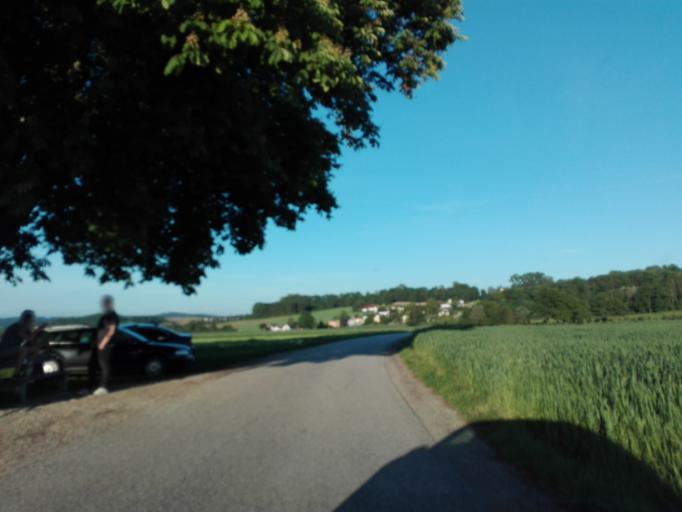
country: AT
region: Upper Austria
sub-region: Politischer Bezirk Urfahr-Umgebung
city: Goldworth
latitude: 48.2808
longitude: 14.1219
